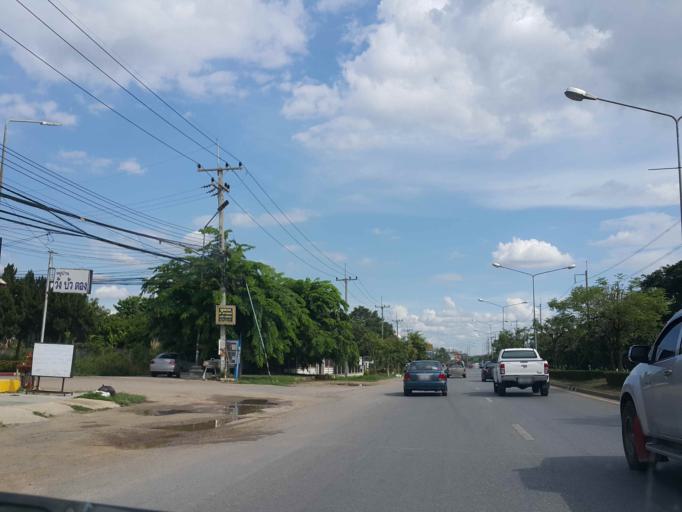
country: TH
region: Chiang Mai
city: San Sai
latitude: 18.8803
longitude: 99.0146
